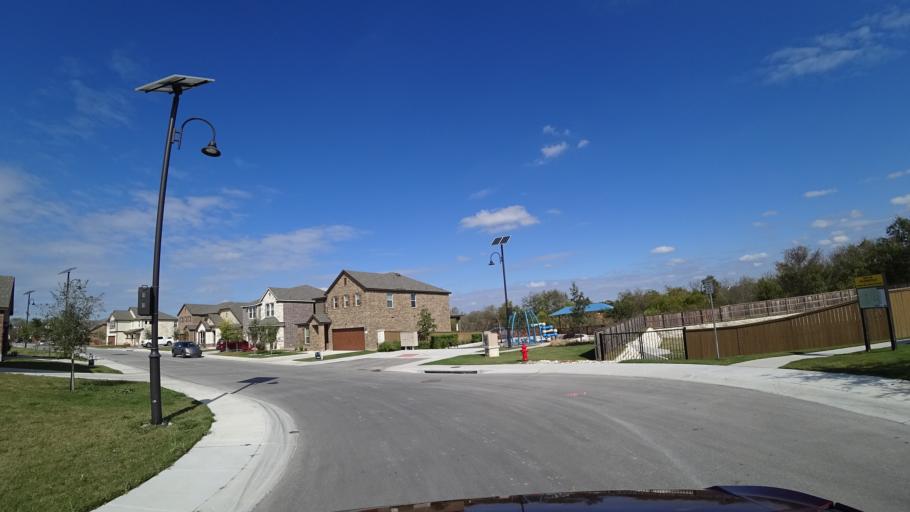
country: US
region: Texas
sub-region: Travis County
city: Pflugerville
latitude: 30.4499
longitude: -97.6274
